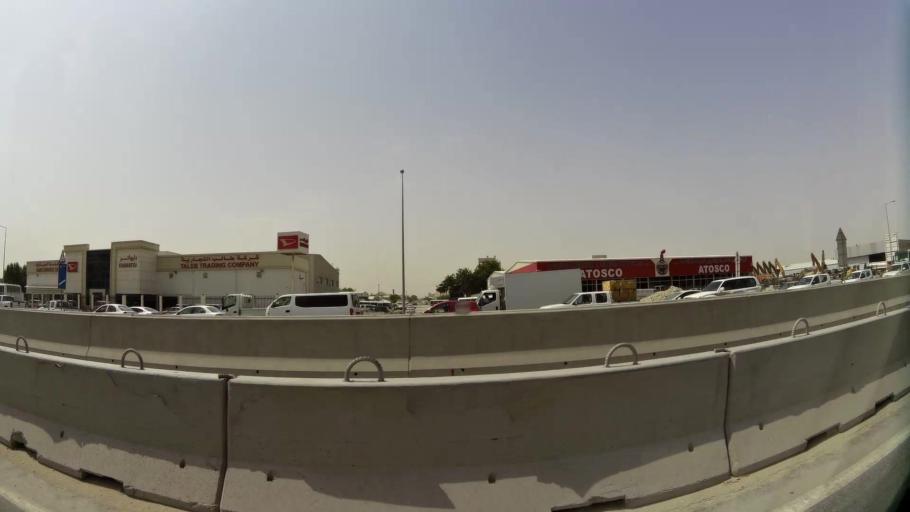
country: QA
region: Al Wakrah
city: Al Wukayr
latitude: 25.1967
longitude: 51.4525
